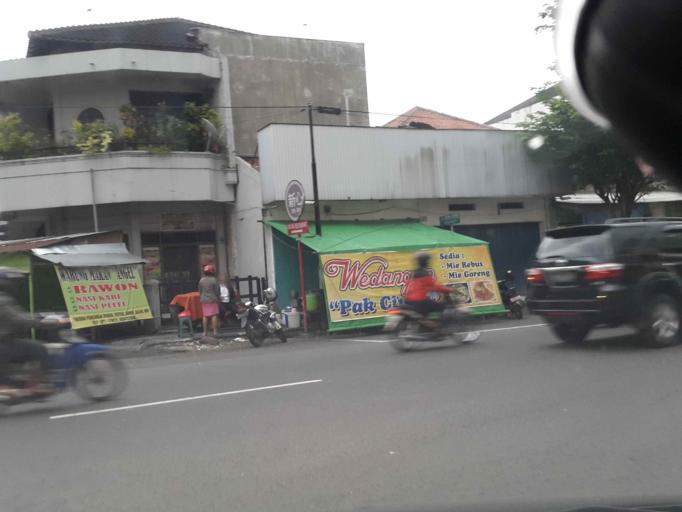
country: ID
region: Central Java
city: Surakarta
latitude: -7.5646
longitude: 110.8283
